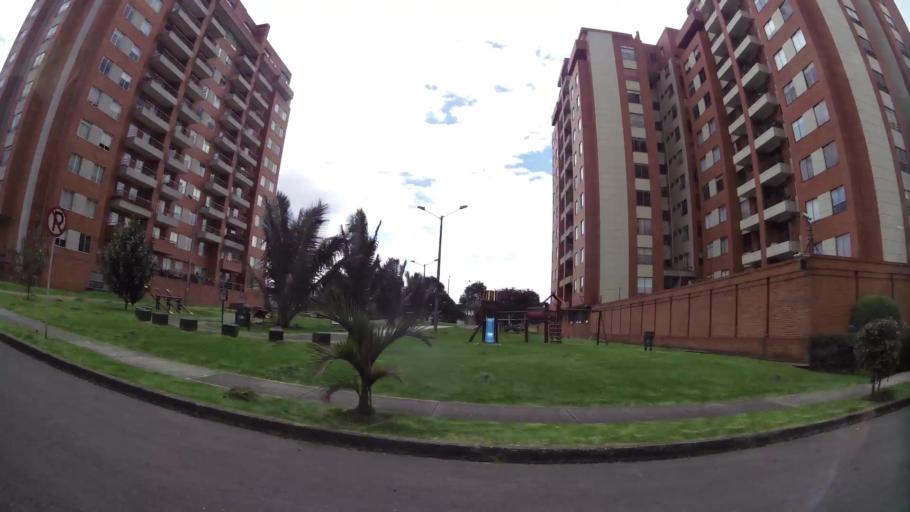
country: CO
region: Bogota D.C.
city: Bogota
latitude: 4.6380
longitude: -74.1018
